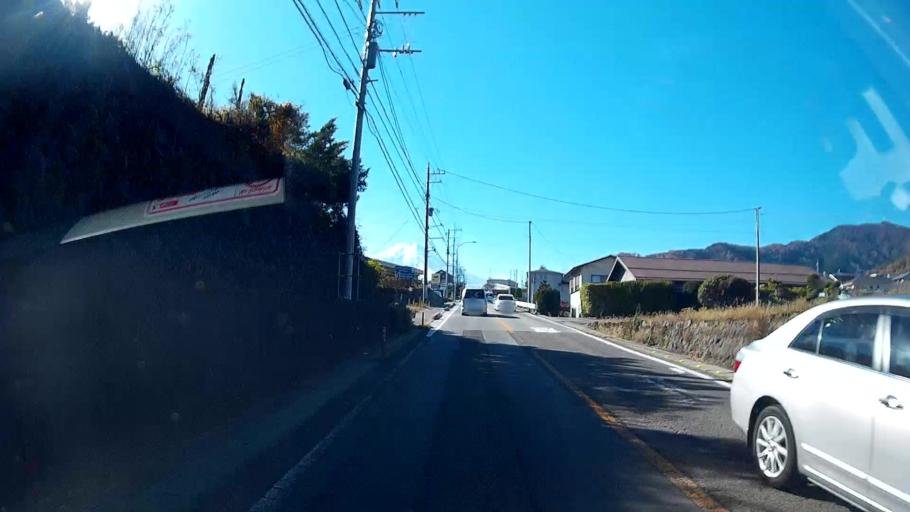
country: JP
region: Yamanashi
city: Otsuki
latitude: 35.5149
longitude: 138.8333
